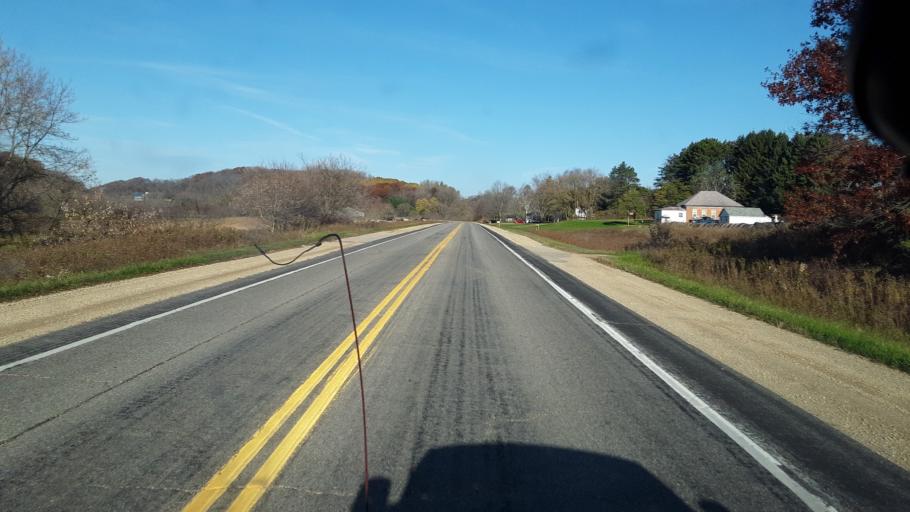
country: US
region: Wisconsin
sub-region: Vernon County
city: Hillsboro
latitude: 43.6567
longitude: -90.3959
